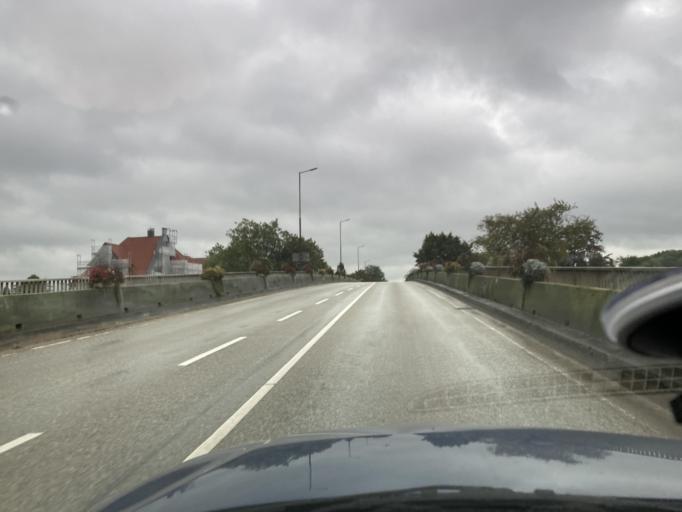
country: DE
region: Schleswig-Holstein
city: Heide
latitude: 54.1953
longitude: 9.0995
